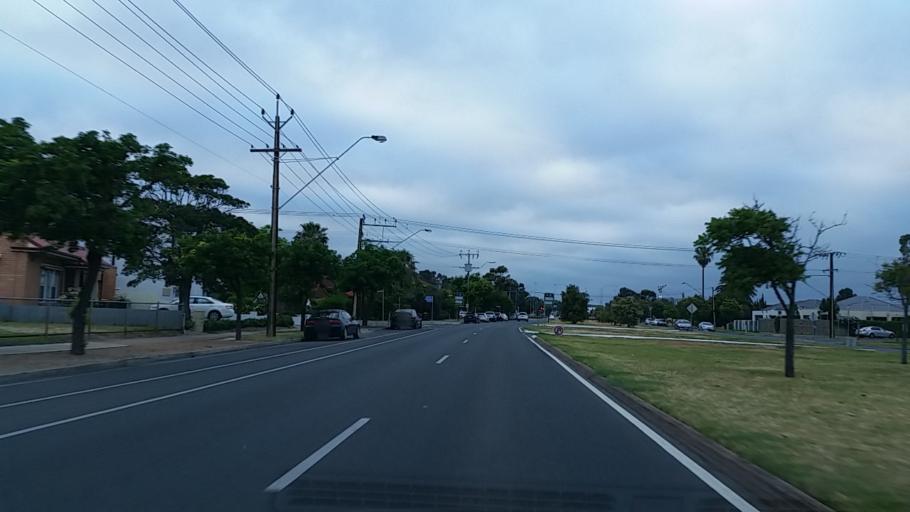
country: AU
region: South Australia
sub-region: City of West Torrens
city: Plympton
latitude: -34.9299
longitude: 138.5425
